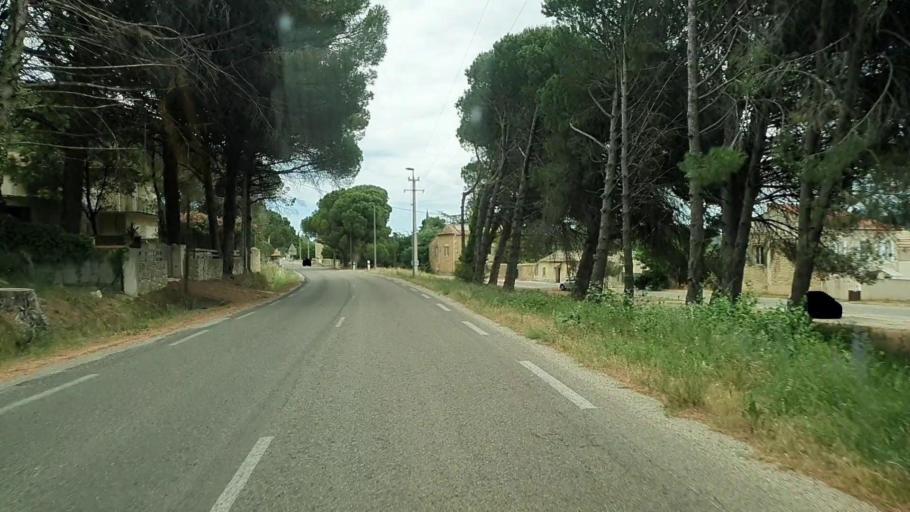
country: FR
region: Languedoc-Roussillon
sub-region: Departement du Gard
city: Tresques
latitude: 44.1222
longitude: 4.5982
